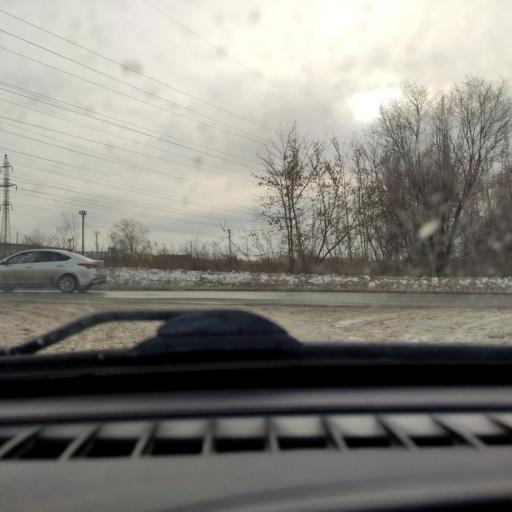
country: RU
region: Samara
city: Tol'yatti
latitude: 53.5815
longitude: 49.2602
